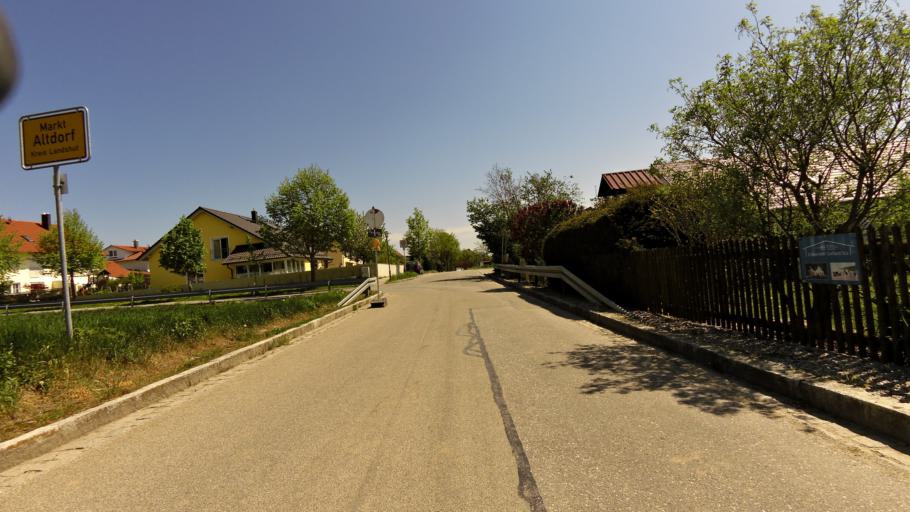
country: DE
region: Bavaria
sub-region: Lower Bavaria
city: Weihmichl
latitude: 48.5629
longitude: 12.0996
